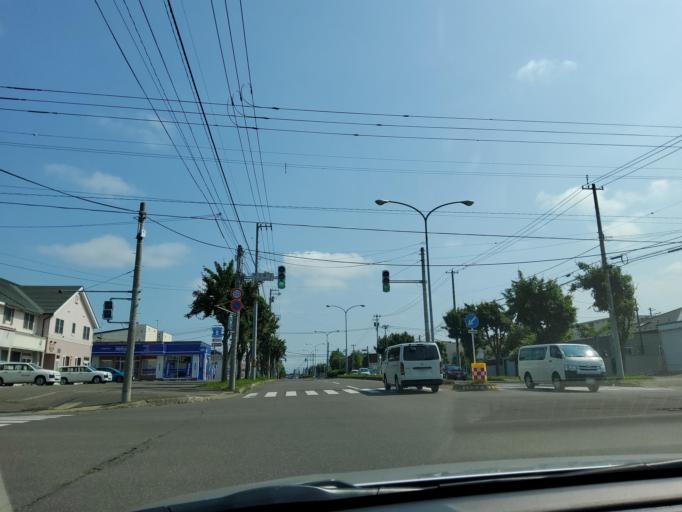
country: JP
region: Hokkaido
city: Obihiro
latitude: 42.9173
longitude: 143.1932
